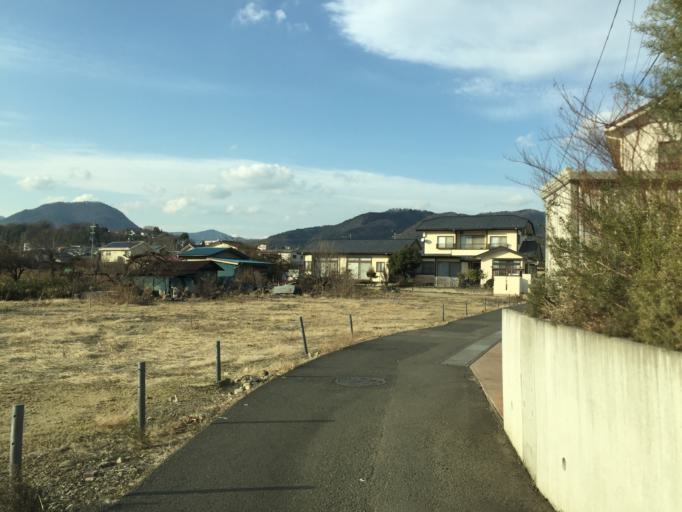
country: JP
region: Fukushima
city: Fukushima-shi
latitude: 37.8247
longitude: 140.4533
